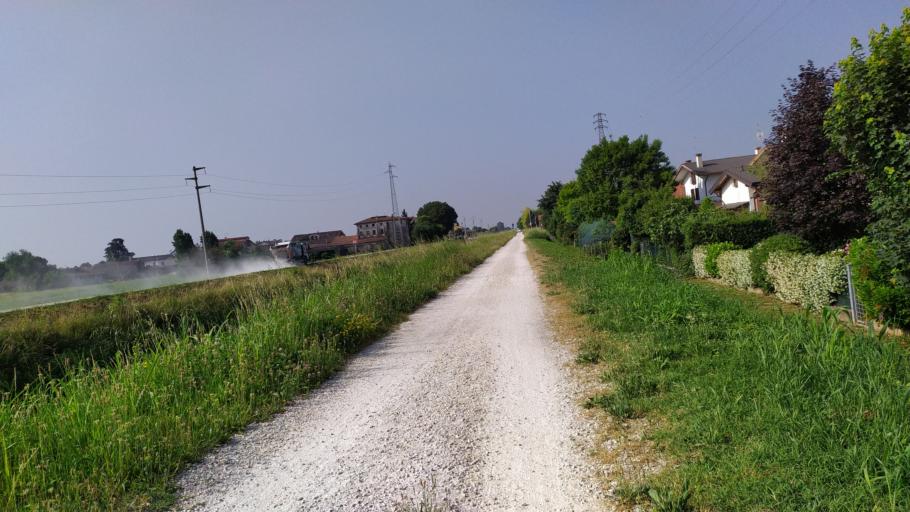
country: IT
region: Veneto
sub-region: Provincia di Padova
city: Camposampiero
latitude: 45.5651
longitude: 11.9378
